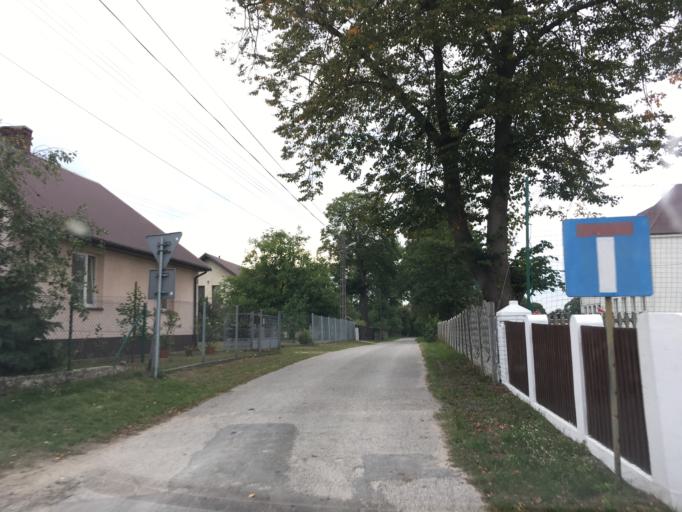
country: PL
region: Lodz Voivodeship
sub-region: Powiat radomszczanski
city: Przedborz
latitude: 51.0028
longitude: 19.8951
